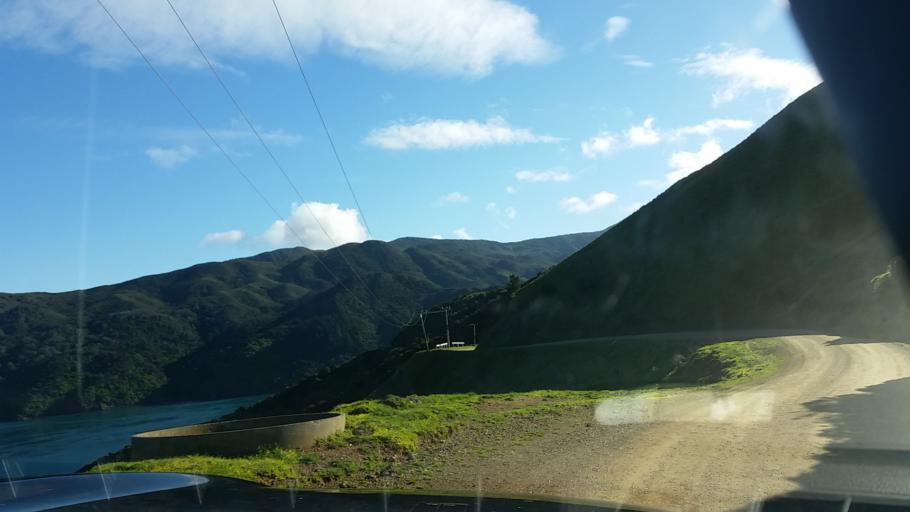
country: NZ
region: Marlborough
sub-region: Marlborough District
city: Picton
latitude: -40.9292
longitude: 173.8394
